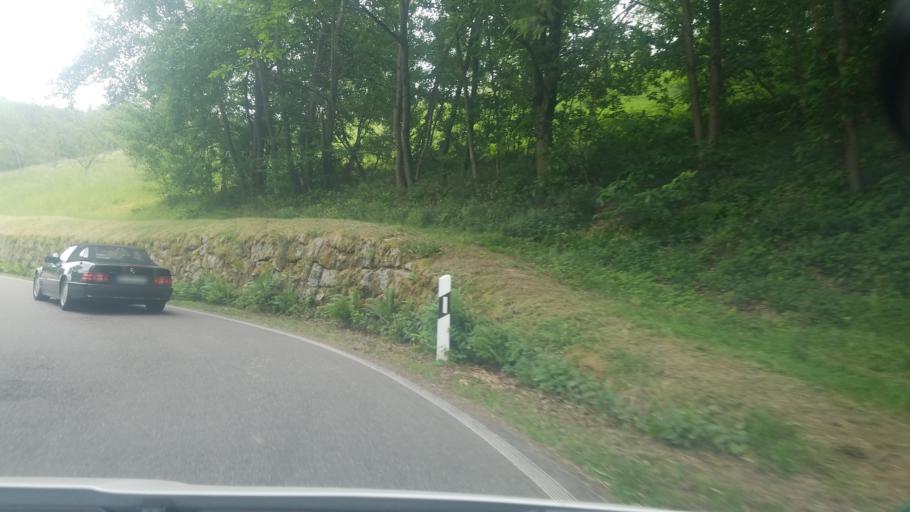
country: DE
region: Baden-Wuerttemberg
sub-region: Freiburg Region
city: Kappelrodeck
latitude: 48.6125
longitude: 8.1111
